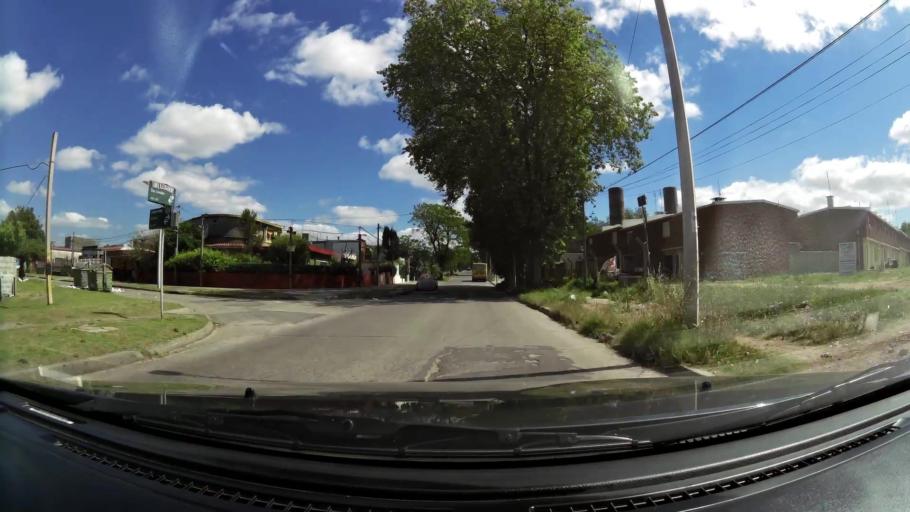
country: UY
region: Montevideo
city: Montevideo
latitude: -34.8579
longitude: -56.1438
